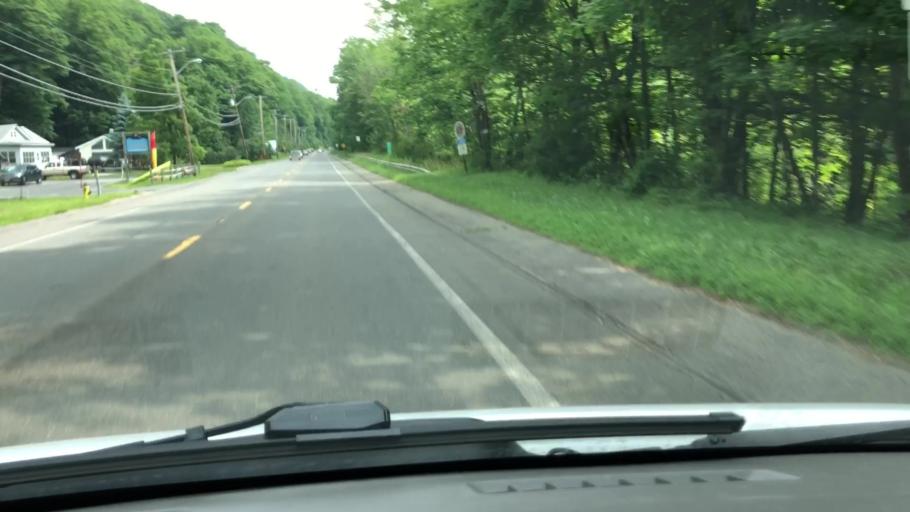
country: US
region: Massachusetts
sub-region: Berkshire County
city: Adams
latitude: 42.5988
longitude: -73.1394
